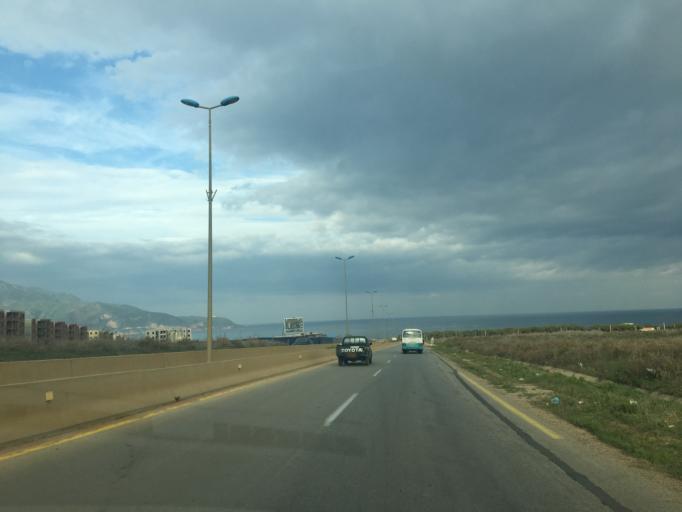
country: DZ
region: Tipaza
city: Tipasa
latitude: 36.5869
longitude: 2.4709
